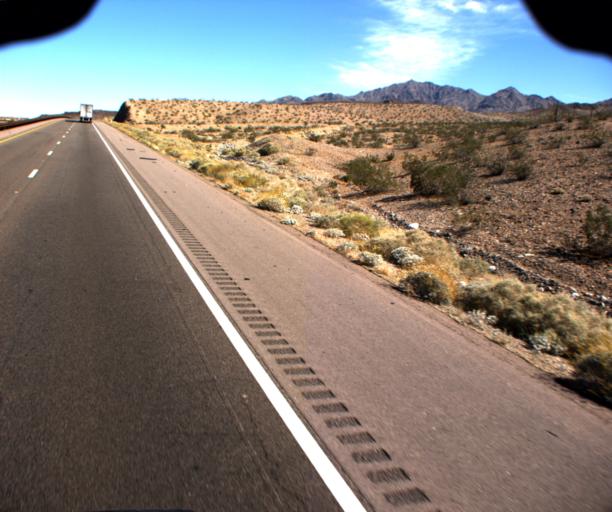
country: US
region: Nevada
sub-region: Clark County
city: Boulder City
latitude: 35.9238
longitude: -114.6323
